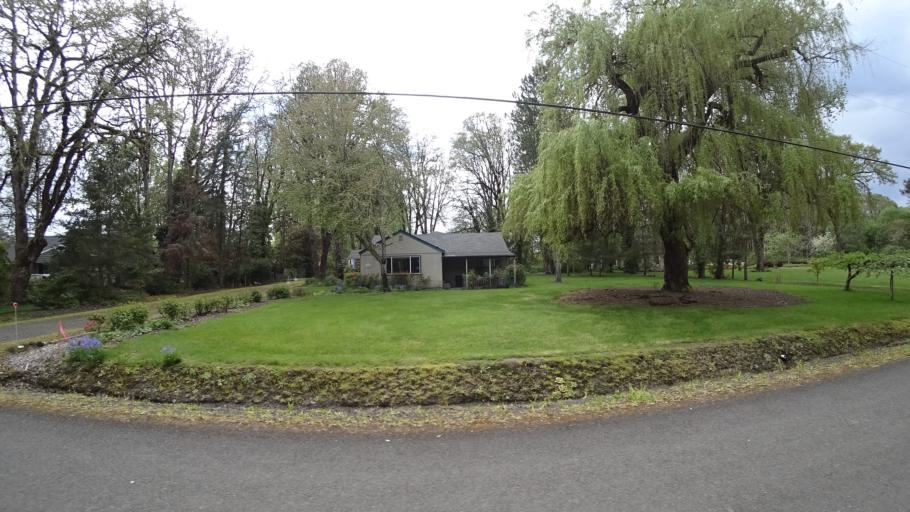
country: US
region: Oregon
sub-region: Washington County
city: Hillsboro
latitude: 45.5580
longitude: -122.9528
